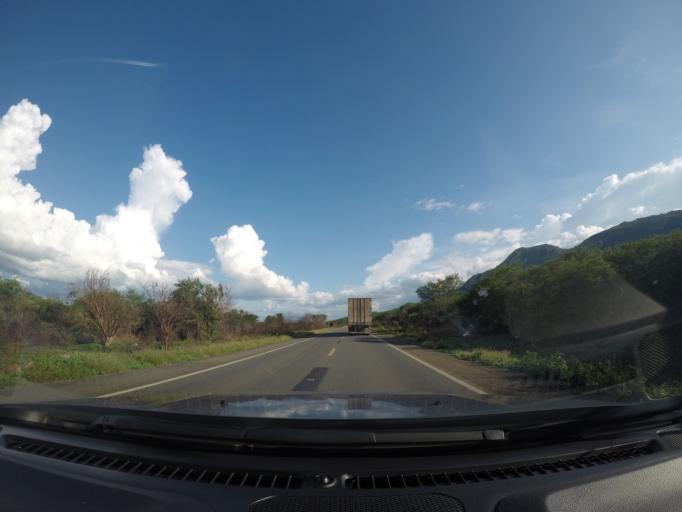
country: BR
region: Bahia
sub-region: Oliveira Dos Brejinhos
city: Oliveira dos Brejinhos
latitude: -12.0596
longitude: -42.9627
